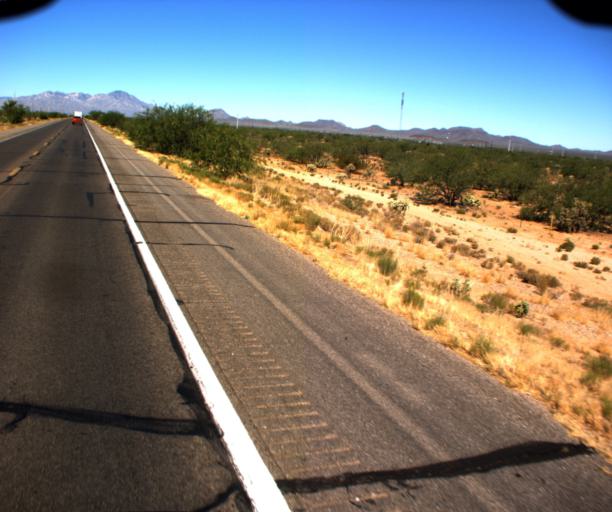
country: US
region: Arizona
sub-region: Pima County
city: Three Points
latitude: 32.0931
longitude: -111.2723
